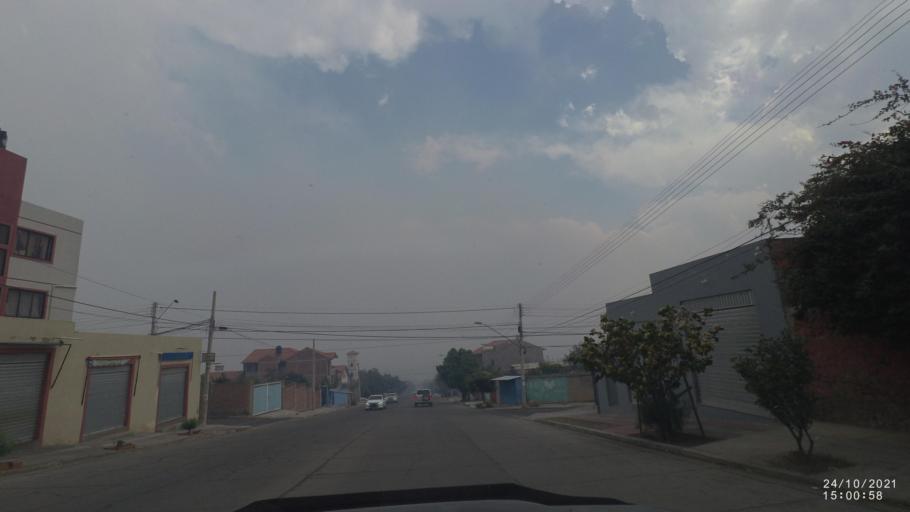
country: BO
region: Cochabamba
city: Cochabamba
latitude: -17.3580
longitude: -66.1535
